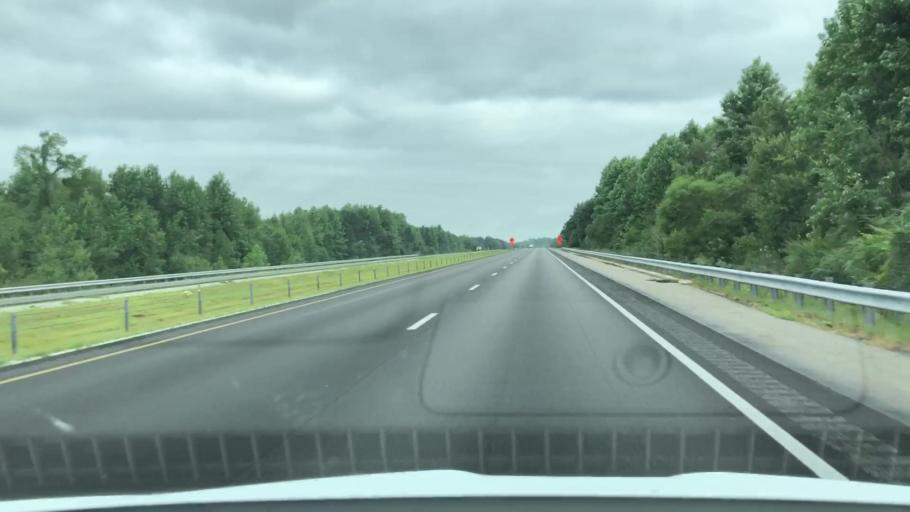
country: US
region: North Carolina
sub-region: Wayne County
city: Fremont
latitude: 35.5709
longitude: -77.9887
